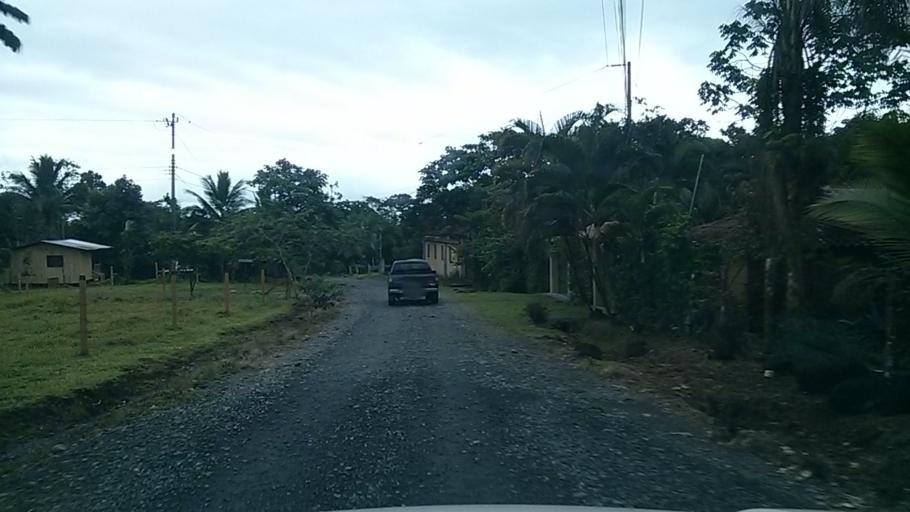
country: CR
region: Limon
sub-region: Canton de Pococi
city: Guapiles
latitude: 10.1636
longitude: -83.7837
